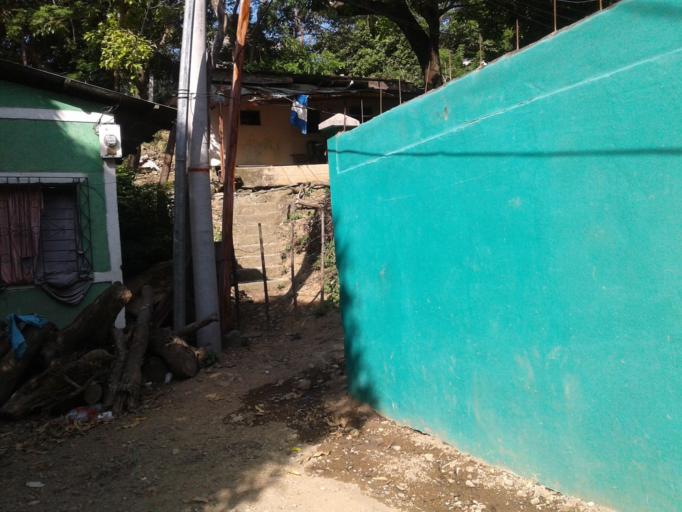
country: NI
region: Rivas
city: San Juan del Sur
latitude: 11.2490
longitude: -85.8726
